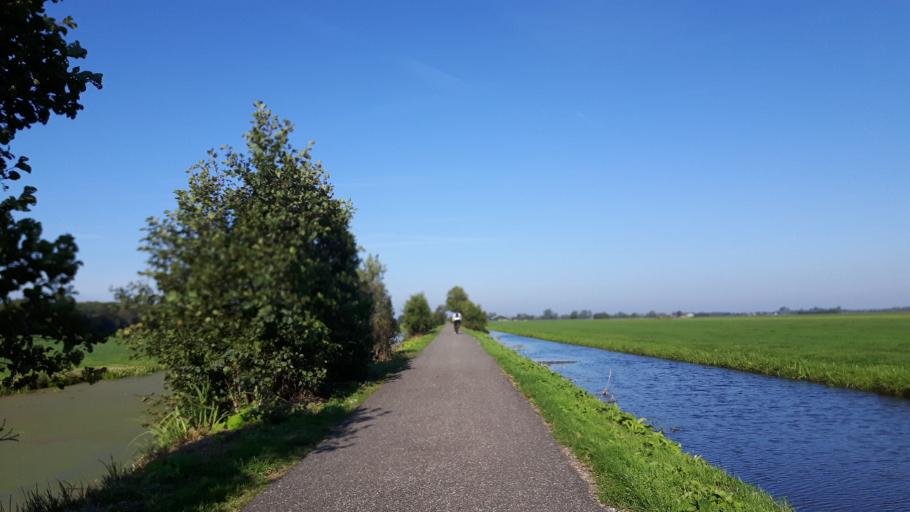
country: NL
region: South Holland
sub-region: Molenwaard
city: Liesveld
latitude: 51.9511
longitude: 4.8096
